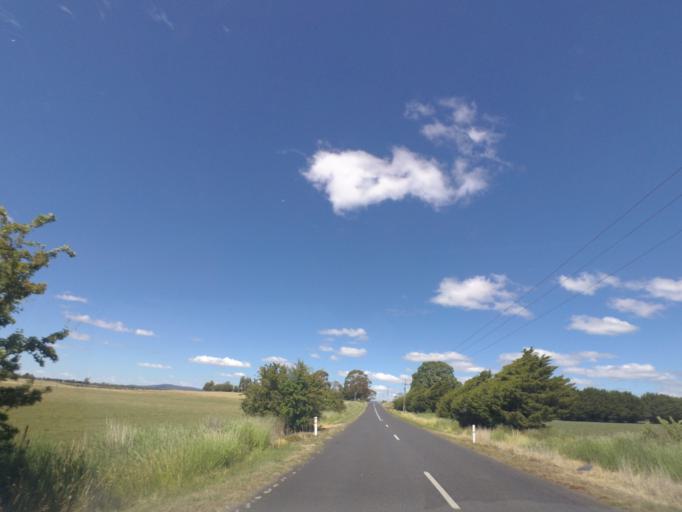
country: AU
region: Victoria
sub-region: Mount Alexander
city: Castlemaine
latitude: -37.2877
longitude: 144.4586
